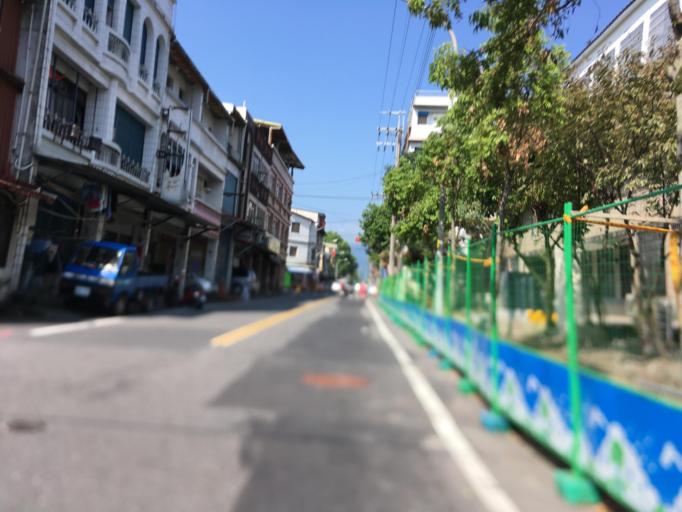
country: TW
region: Taiwan
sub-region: Yilan
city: Yilan
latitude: 24.6675
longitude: 121.6532
